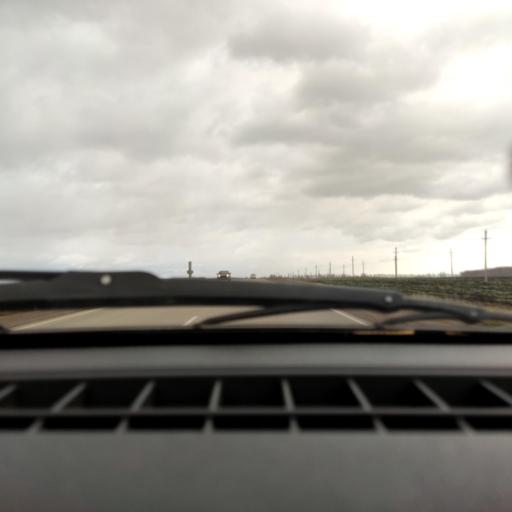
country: RU
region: Bashkortostan
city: Iglino
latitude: 54.7567
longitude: 56.2792
